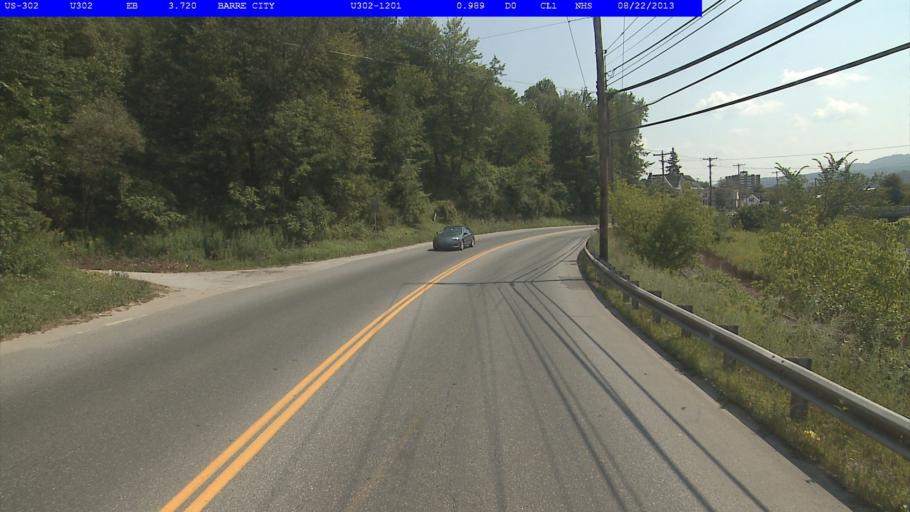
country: US
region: Vermont
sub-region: Washington County
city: Barre
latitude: 44.2108
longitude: -72.5164
